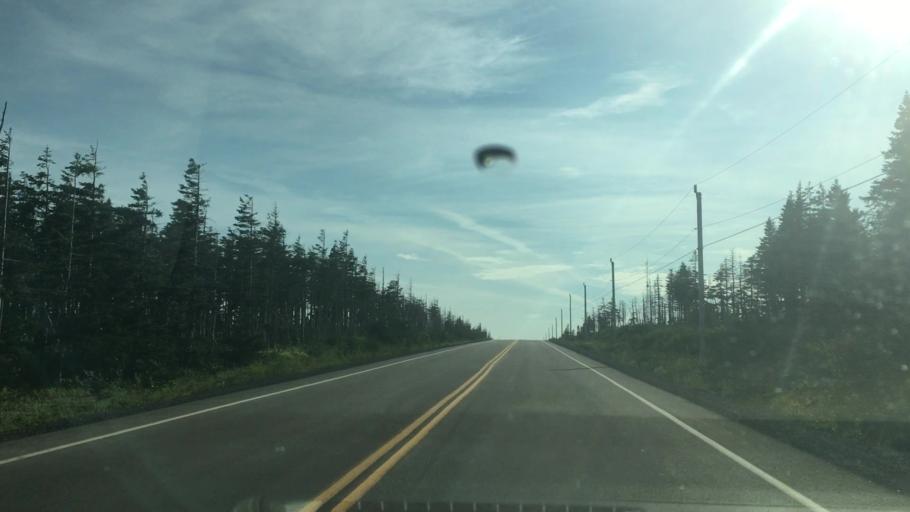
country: CA
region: Nova Scotia
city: Sydney Mines
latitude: 46.8219
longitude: -60.6639
